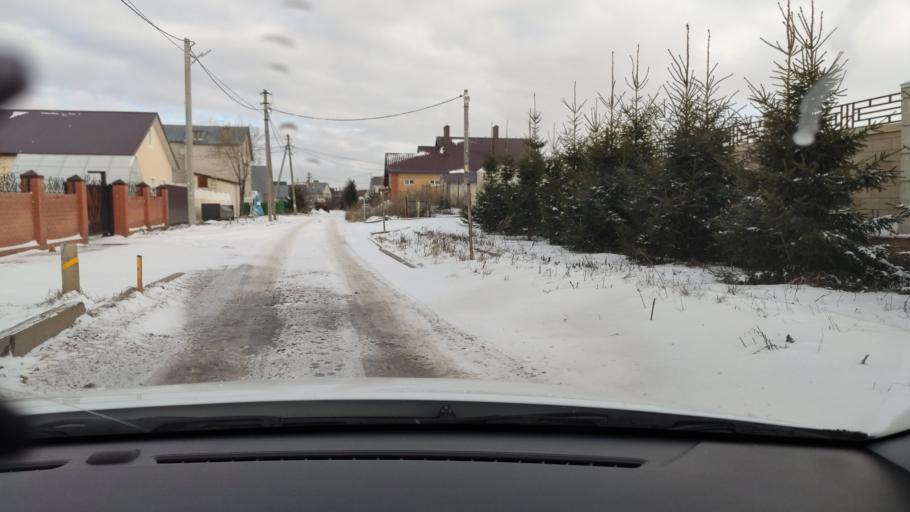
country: RU
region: Tatarstan
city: Stolbishchi
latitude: 55.7698
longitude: 49.2704
